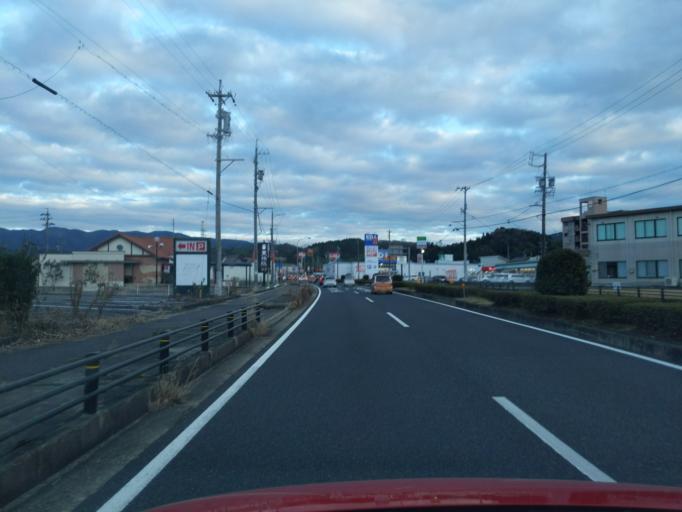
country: JP
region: Gifu
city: Mizunami
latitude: 35.3574
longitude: 137.2446
